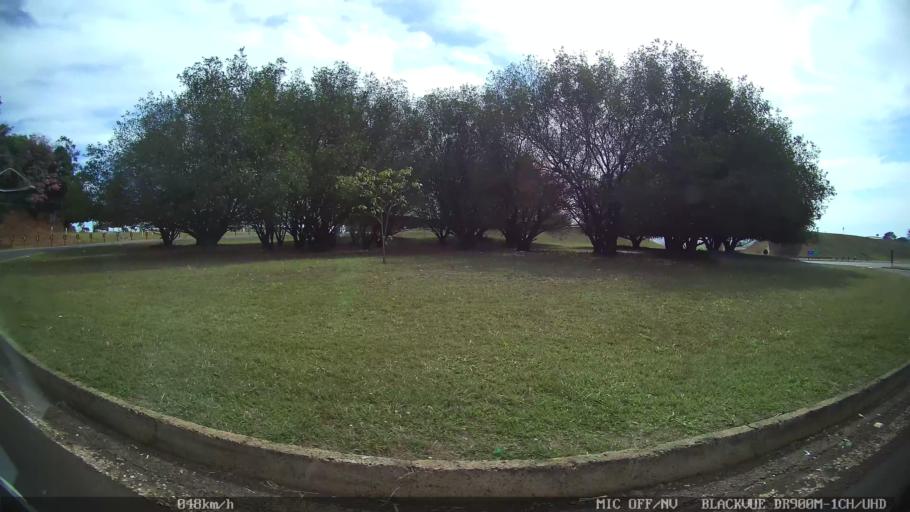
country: BR
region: Sao Paulo
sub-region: Matao
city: Matao
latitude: -21.6420
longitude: -48.3948
